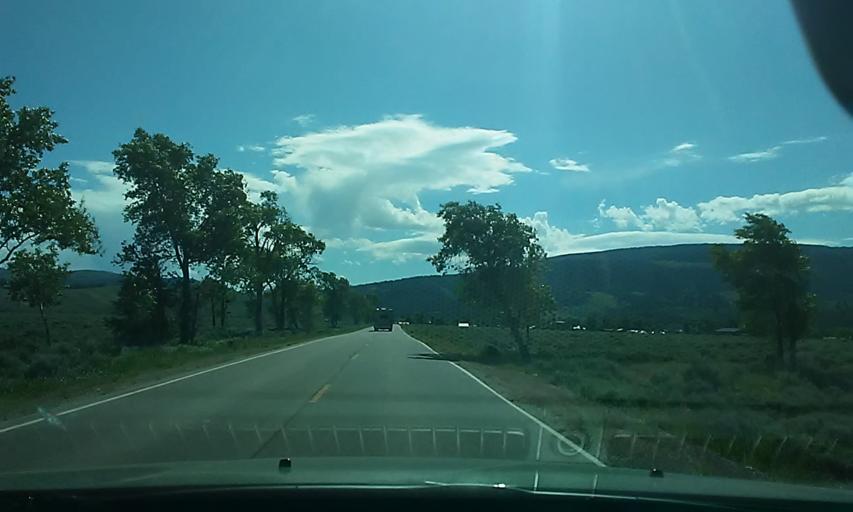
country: US
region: Wyoming
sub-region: Teton County
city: Jackson
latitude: 43.6251
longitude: -110.6360
